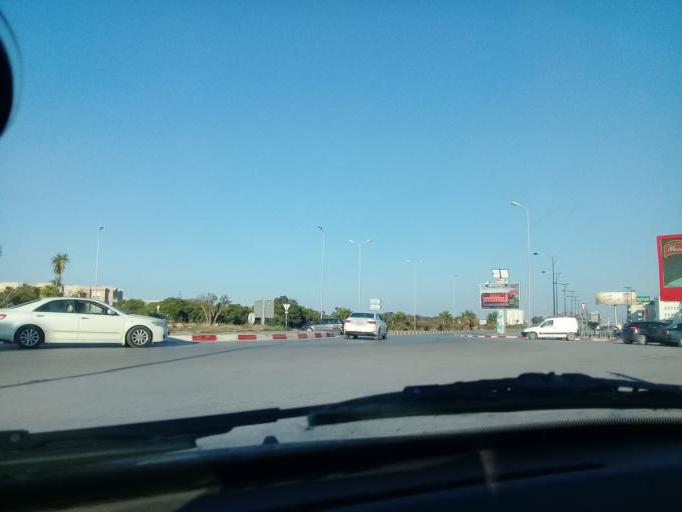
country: TN
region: Tunis
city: La Goulette
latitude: 36.8479
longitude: 10.2800
